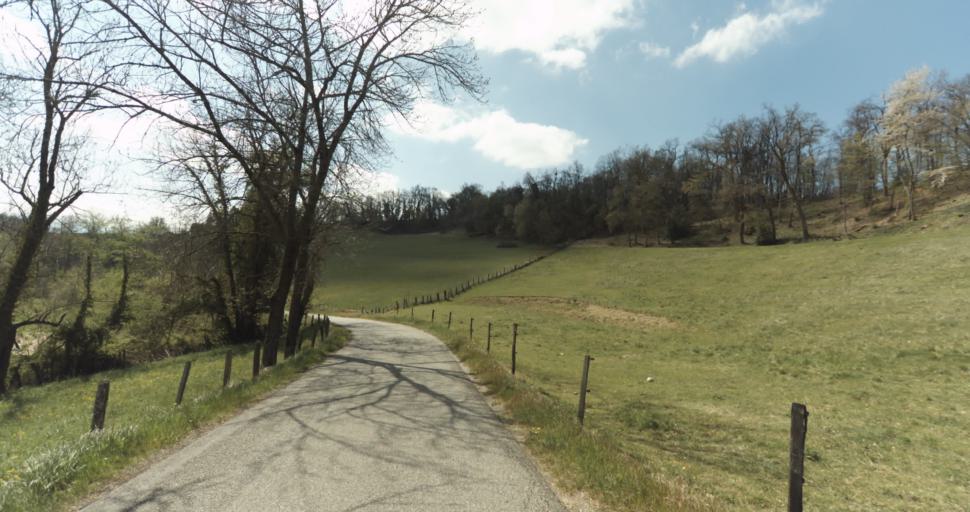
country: FR
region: Rhone-Alpes
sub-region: Departement de l'Isere
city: Saint-Marcellin
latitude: 45.1644
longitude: 5.3094
